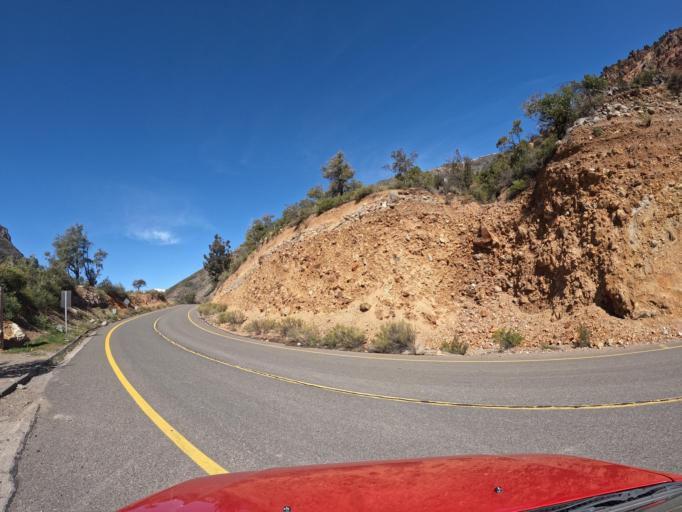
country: CL
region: Maule
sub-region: Provincia de Linares
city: Colbun
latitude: -35.8236
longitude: -70.7626
